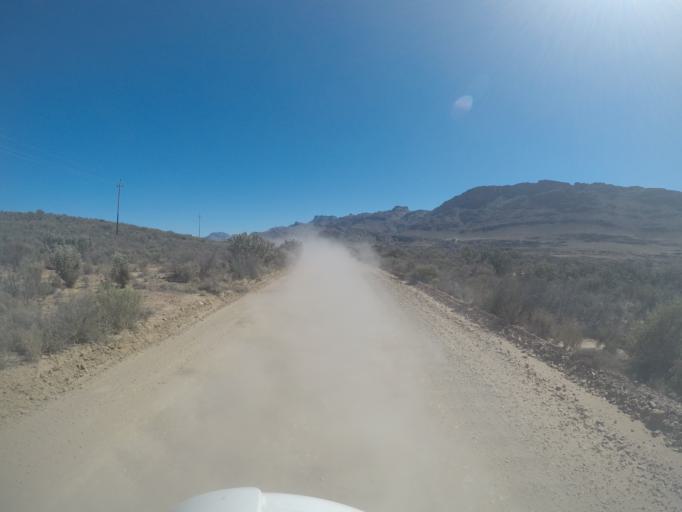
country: ZA
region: Western Cape
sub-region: West Coast District Municipality
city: Clanwilliam
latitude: -32.4995
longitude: 19.2760
